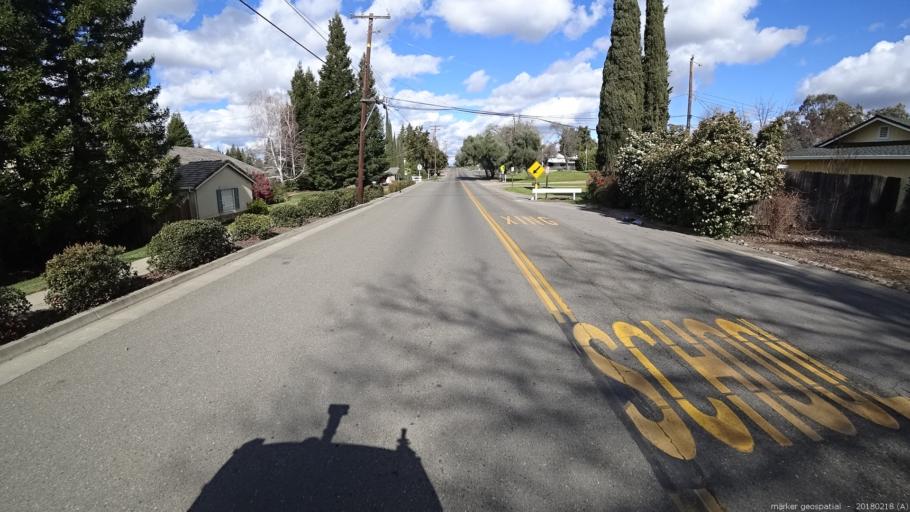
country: US
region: California
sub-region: Sacramento County
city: Orangevale
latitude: 38.6838
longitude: -121.2162
